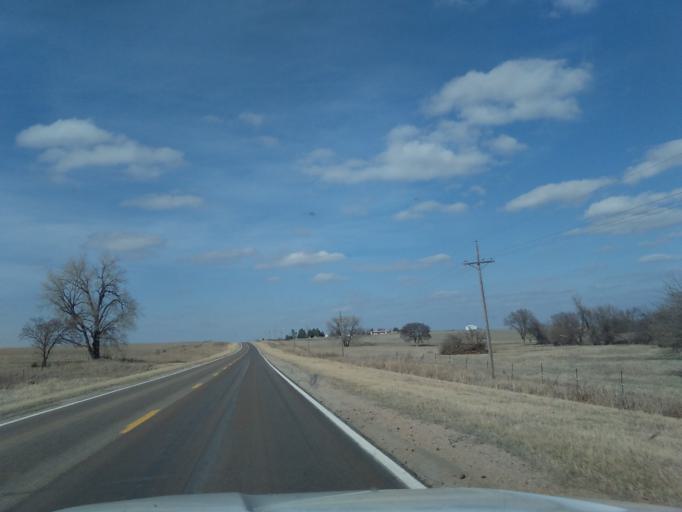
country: US
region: Nebraska
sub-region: Jefferson County
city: Fairbury
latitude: 40.0760
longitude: -96.9352
